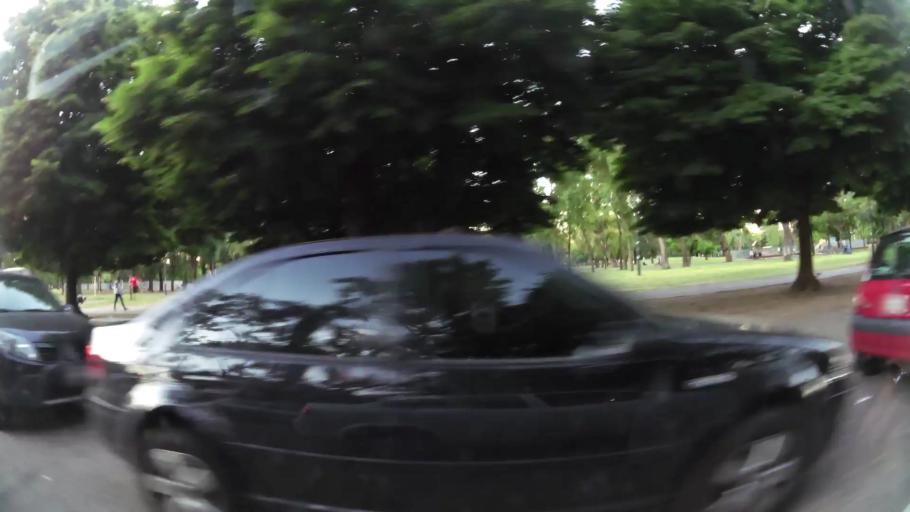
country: AR
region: Buenos Aires F.D.
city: Colegiales
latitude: -34.5521
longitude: -58.4803
